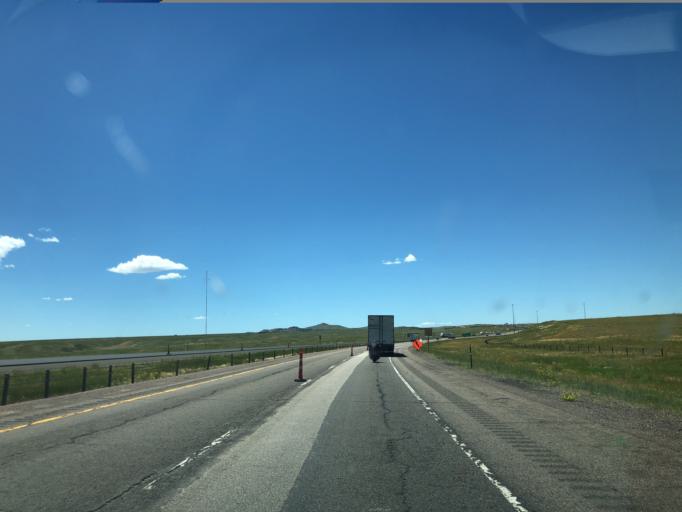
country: US
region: Wyoming
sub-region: Laramie County
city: Cheyenne
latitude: 41.0977
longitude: -105.1027
